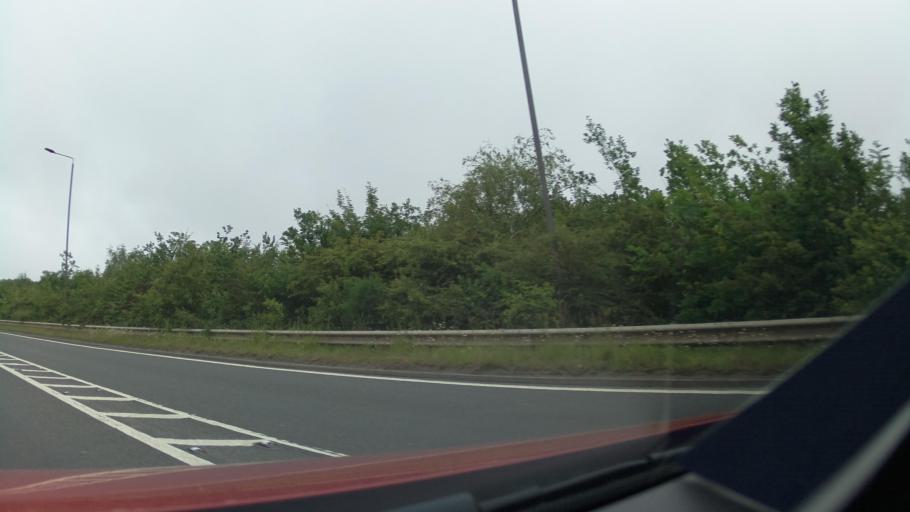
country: GB
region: England
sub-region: Derbyshire
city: Swadlincote
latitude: 52.7558
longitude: -1.5770
